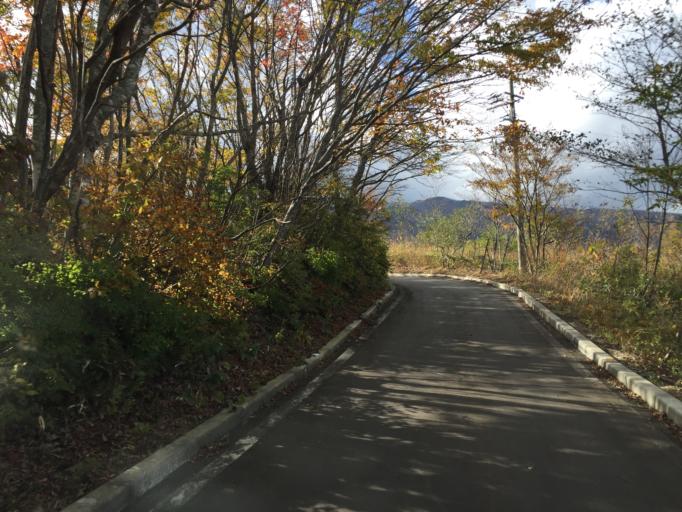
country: JP
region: Fukushima
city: Fukushima-shi
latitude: 37.7337
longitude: 140.3166
